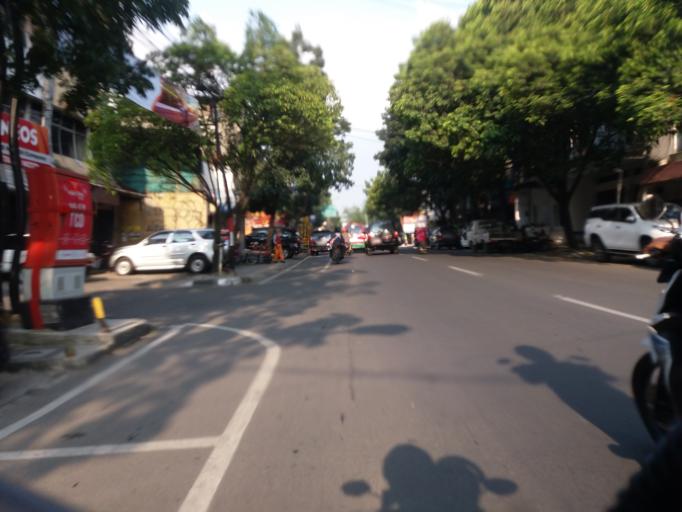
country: ID
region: West Java
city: Bandung
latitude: -6.9281
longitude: 107.6151
